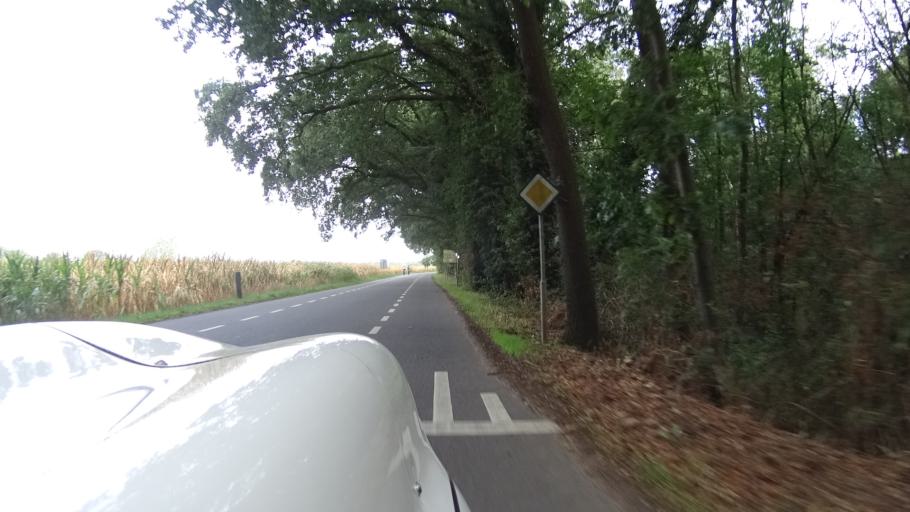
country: NL
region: Limburg
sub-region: Gemeente Venray
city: Venray
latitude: 51.5575
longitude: 6.0445
